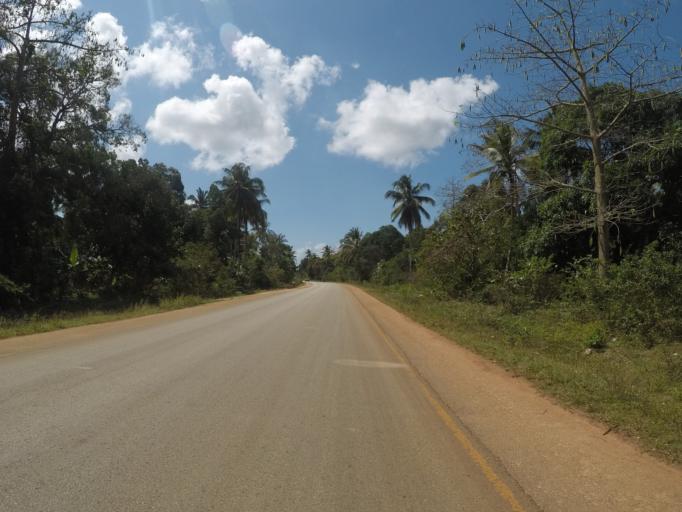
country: TZ
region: Zanzibar Central/South
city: Koani
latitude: -6.1683
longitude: 39.3303
